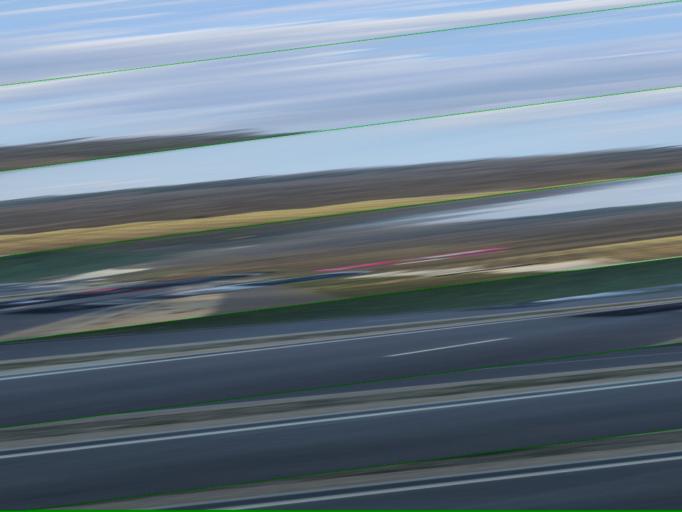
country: FR
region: Ile-de-France
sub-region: Departement des Yvelines
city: Plaisir
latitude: 48.8097
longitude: 1.9602
